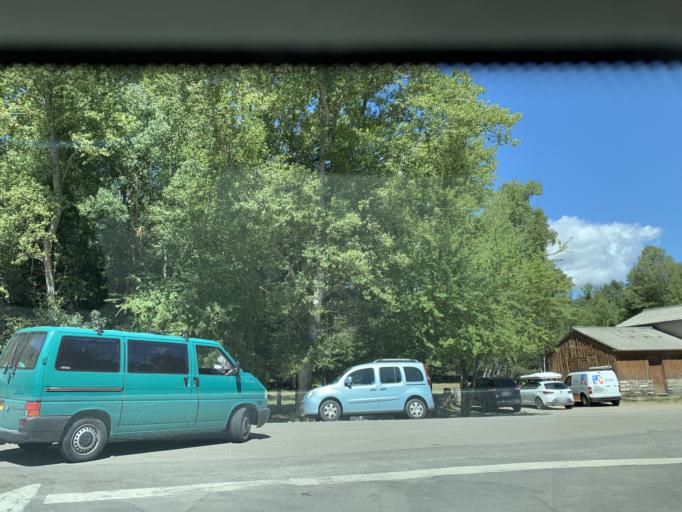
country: ES
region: Aragon
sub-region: Provincia de Huesca
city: Biescas
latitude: 42.5790
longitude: -0.3223
